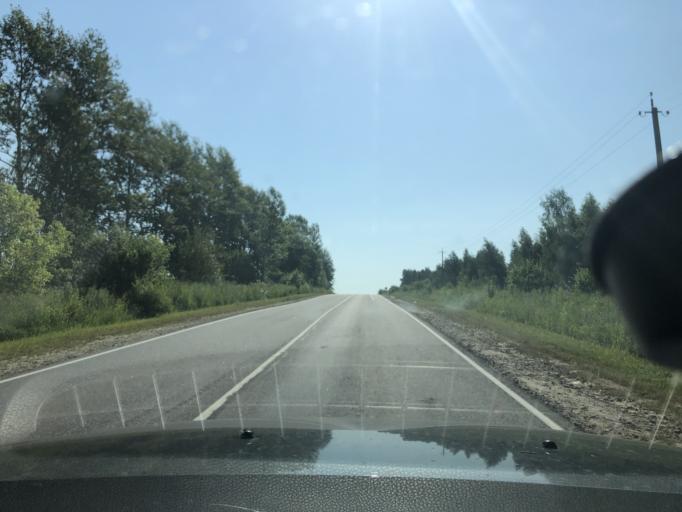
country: RU
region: Tula
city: Dubna
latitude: 54.1438
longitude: 36.9944
